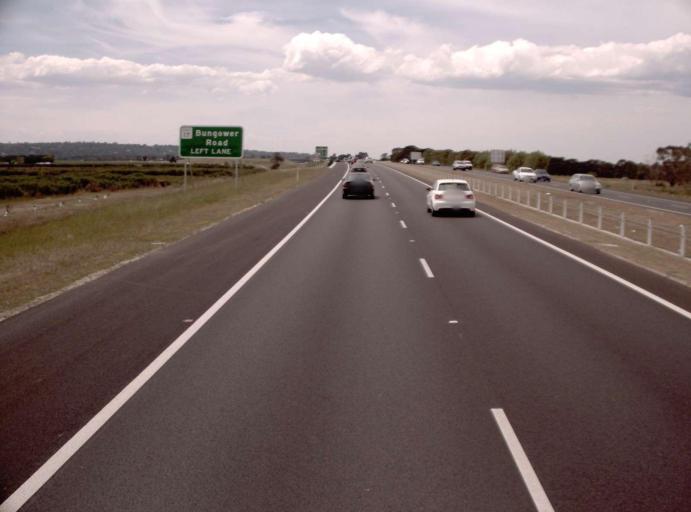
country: AU
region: Victoria
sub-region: Mornington Peninsula
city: Moorooduc
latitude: -38.2432
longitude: 145.1221
